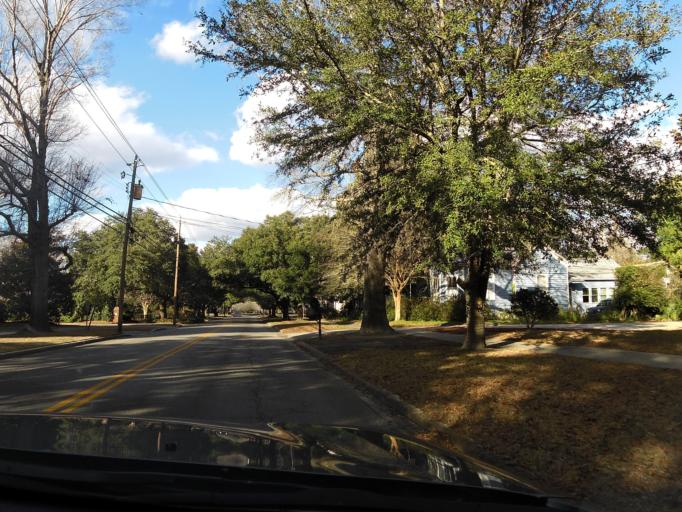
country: US
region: South Carolina
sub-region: Clarendon County
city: Manning
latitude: 33.7002
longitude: -80.2105
